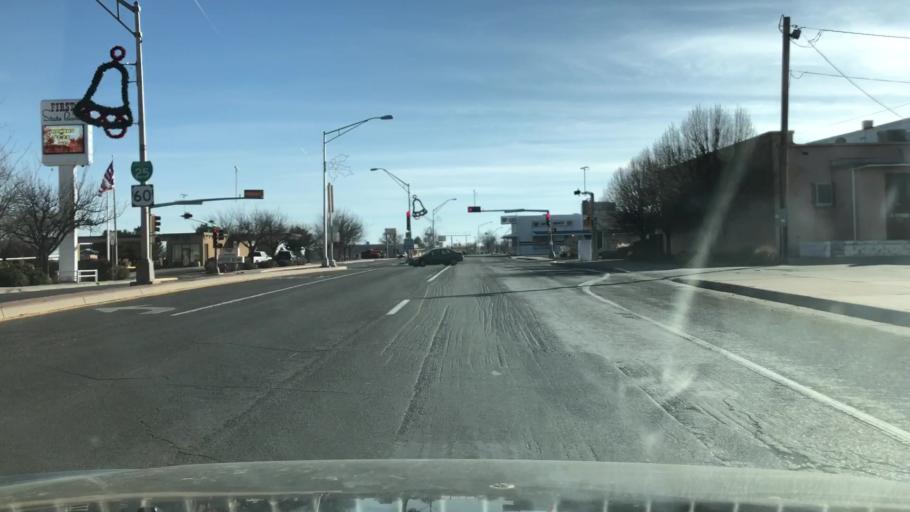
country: US
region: New Mexico
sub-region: Socorro County
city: Socorro
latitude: 34.0580
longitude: -106.8918
